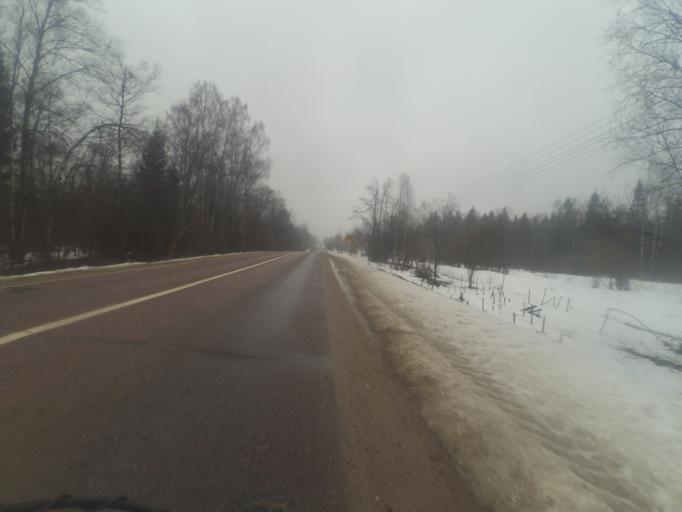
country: RU
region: Moskovskaya
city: Avtopoligon
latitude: 56.2619
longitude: 37.2760
